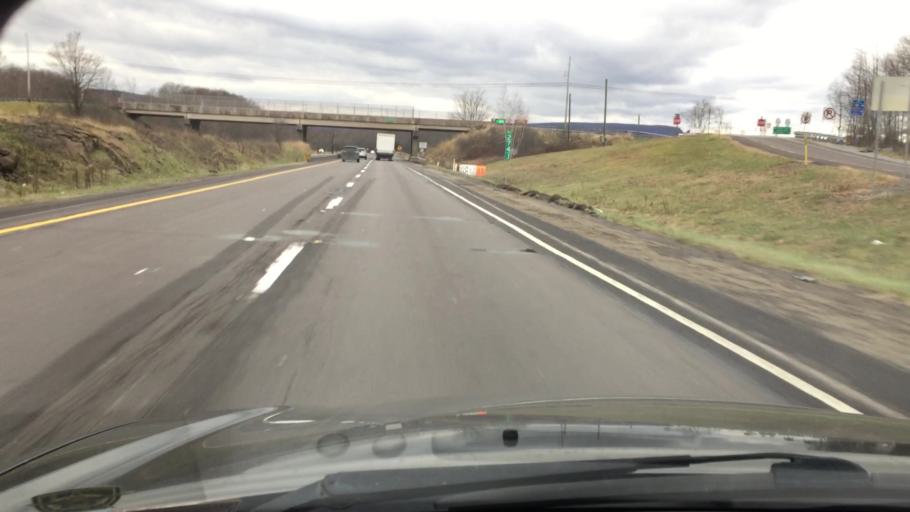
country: US
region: Pennsylvania
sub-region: Luzerne County
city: White Haven
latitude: 41.0608
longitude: -75.7468
